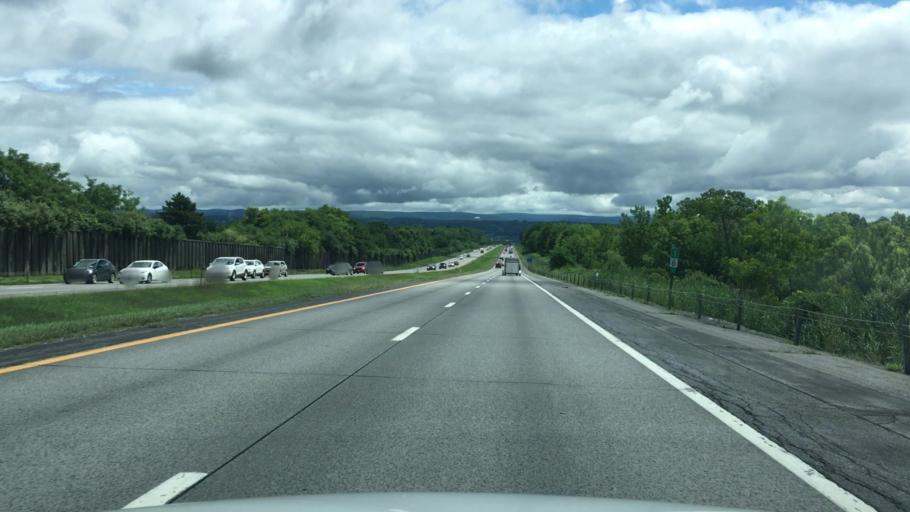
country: US
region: New York
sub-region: Albany County
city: Cohoes
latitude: 42.7563
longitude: -73.7342
